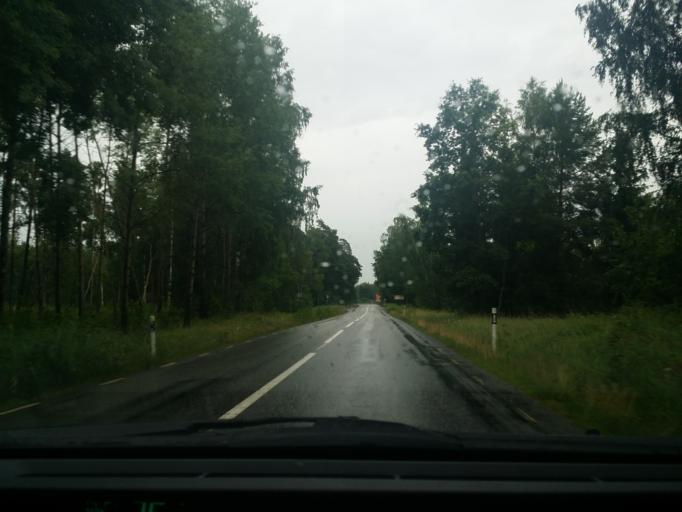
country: SE
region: Vaestmanland
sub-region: Arboga Kommun
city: Arboga
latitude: 59.4161
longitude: 15.7140
